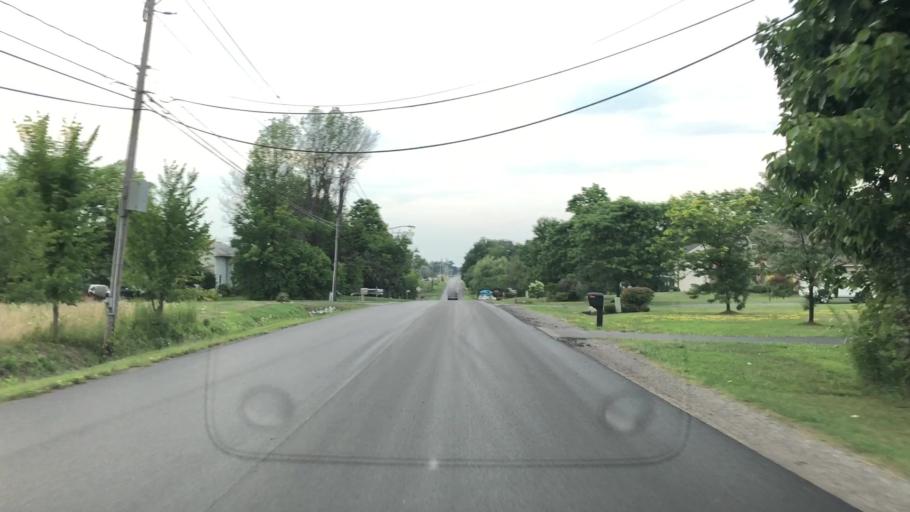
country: US
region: New York
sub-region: Erie County
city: Elma Center
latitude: 42.8274
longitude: -78.6059
